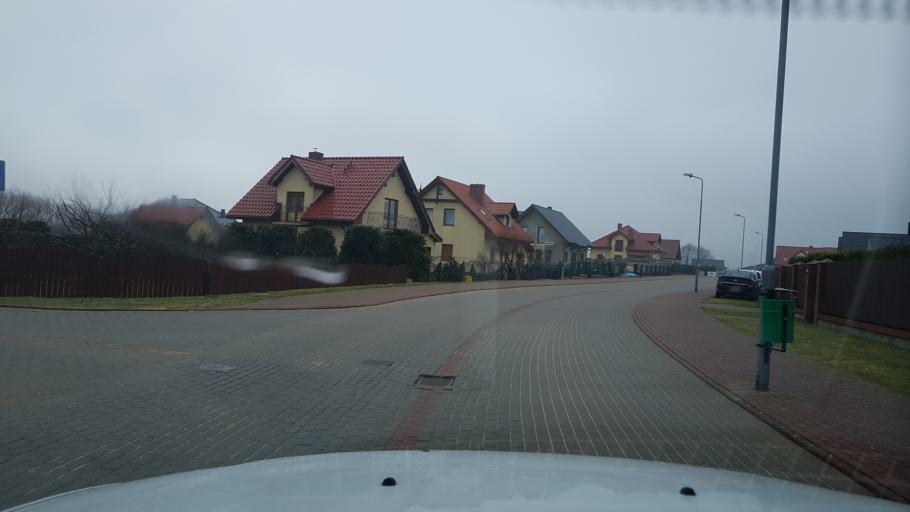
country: PL
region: West Pomeranian Voivodeship
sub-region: Powiat drawski
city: Czaplinek
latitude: 53.5668
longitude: 16.2352
